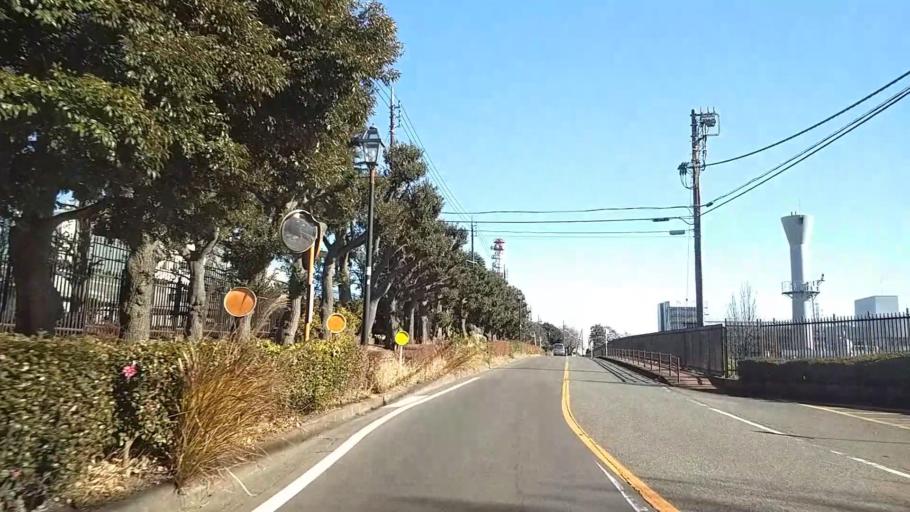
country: JP
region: Kanagawa
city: Yokohama
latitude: 35.4649
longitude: 139.5690
